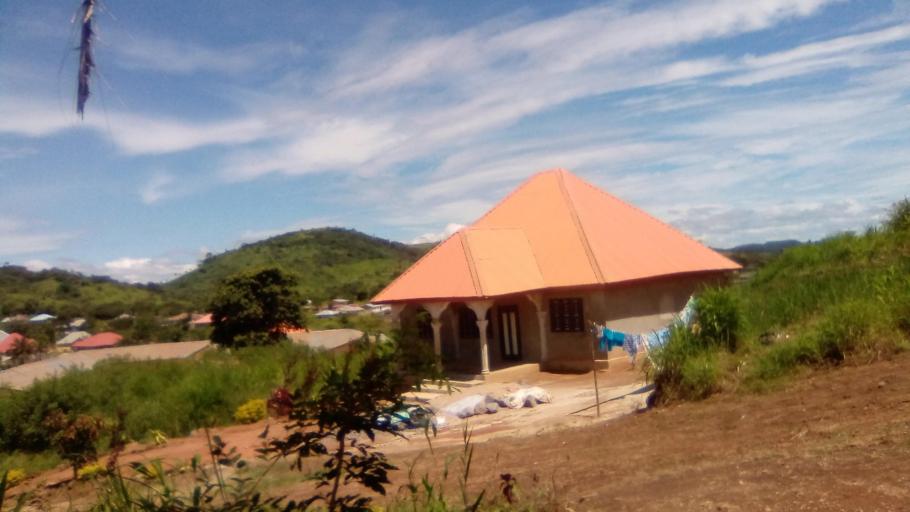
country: SL
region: Eastern Province
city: Simbakoro
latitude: 8.6326
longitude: -10.9962
